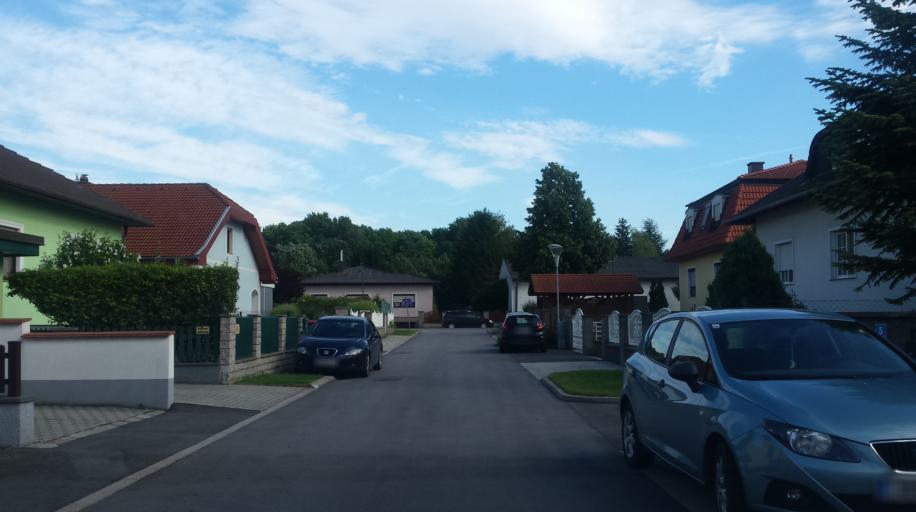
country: AT
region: Burgenland
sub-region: Eisenstadt-Umgebung
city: Leithaprodersdorf
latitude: 47.9440
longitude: 16.4813
